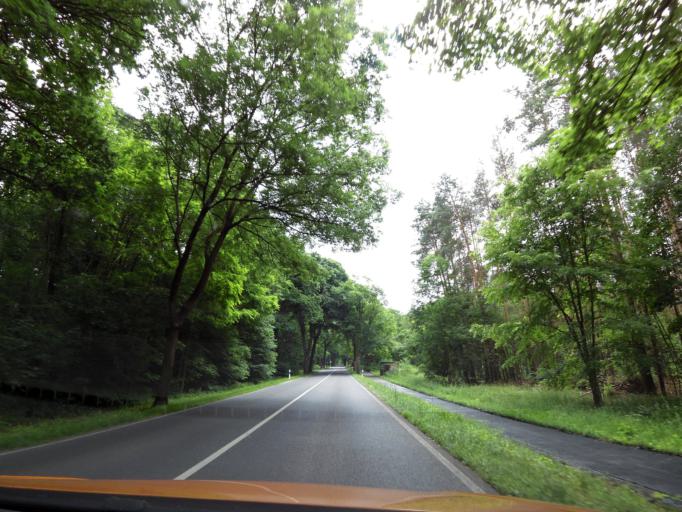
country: DE
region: Brandenburg
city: Zossen
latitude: 52.1856
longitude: 13.4642
